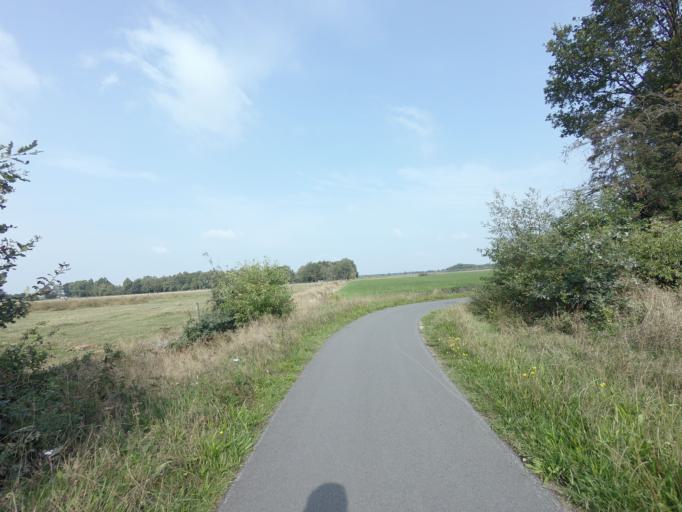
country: NL
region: Drenthe
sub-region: Gemeente Assen
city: Assen
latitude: 52.9361
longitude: 6.5718
